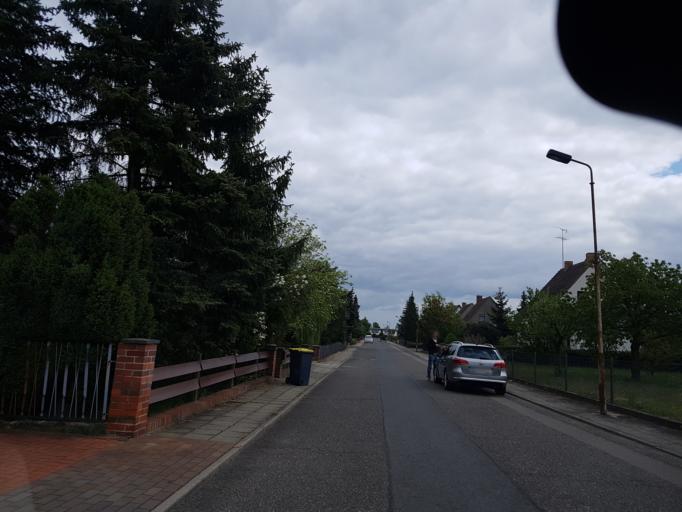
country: DE
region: Brandenburg
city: Altdobern
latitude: 51.6461
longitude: 14.0203
